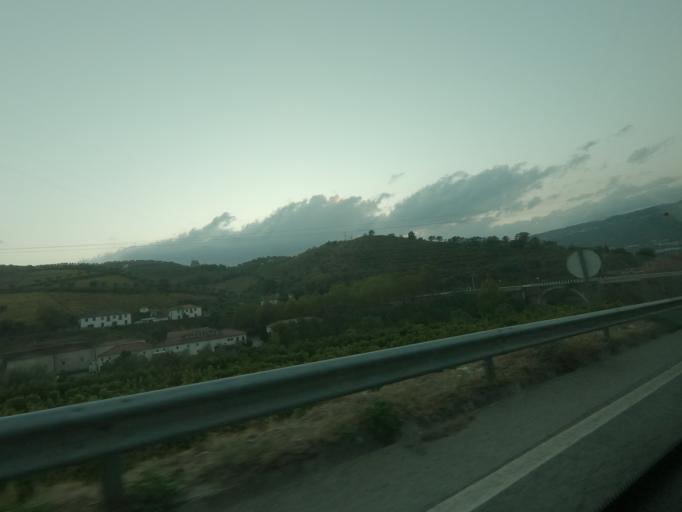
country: PT
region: Vila Real
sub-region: Peso da Regua
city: Peso da Regua
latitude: 41.1513
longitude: -7.7811
